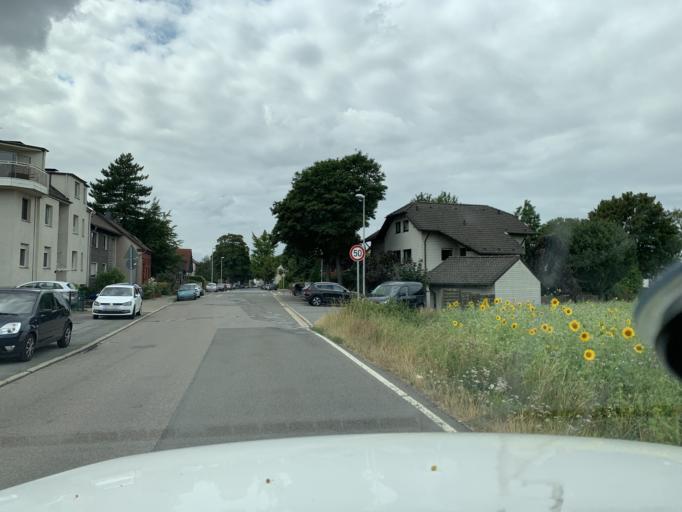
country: DE
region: North Rhine-Westphalia
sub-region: Regierungsbezirk Dusseldorf
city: Oberhausen
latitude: 51.4555
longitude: 6.9114
